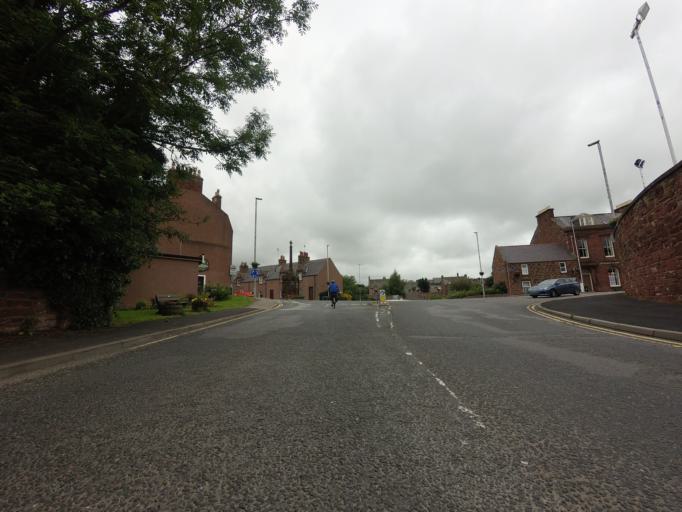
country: GB
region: Scotland
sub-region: Aberdeenshire
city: Turriff
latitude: 57.5372
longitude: -2.4639
